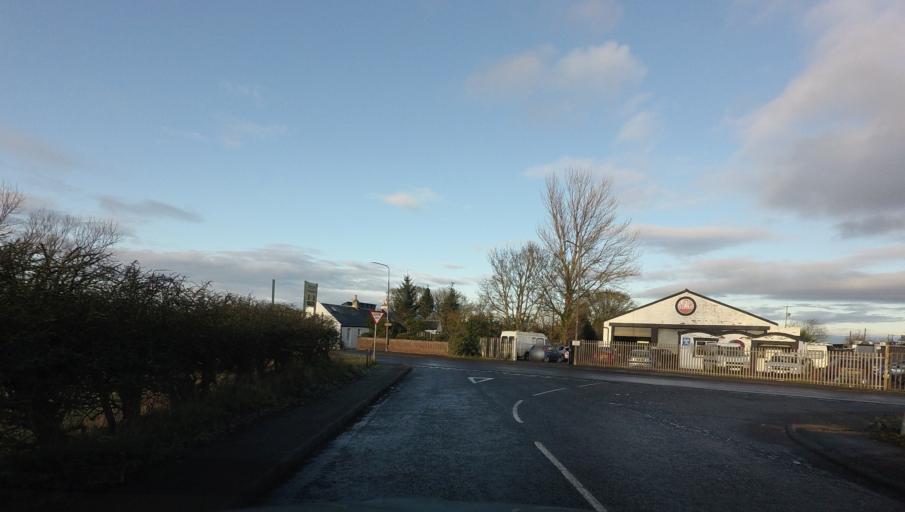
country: GB
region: Scotland
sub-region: West Lothian
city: East Calder
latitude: 55.8979
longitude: -3.4458
